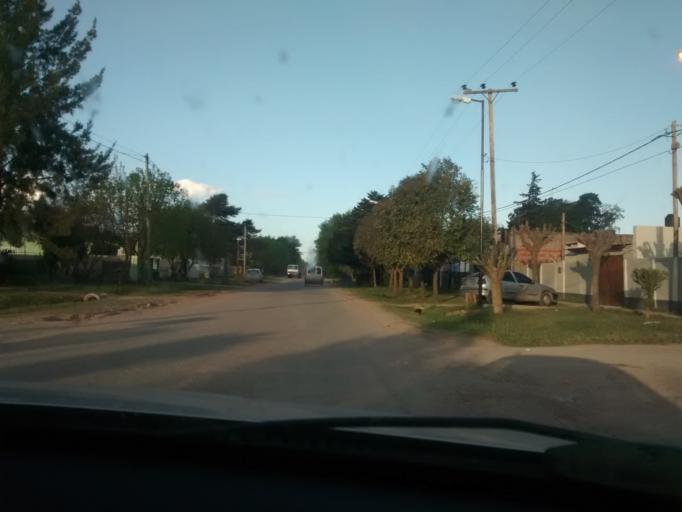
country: AR
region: Buenos Aires
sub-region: Partido de Brandsen
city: Brandsen
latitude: -35.1742
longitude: -58.2208
